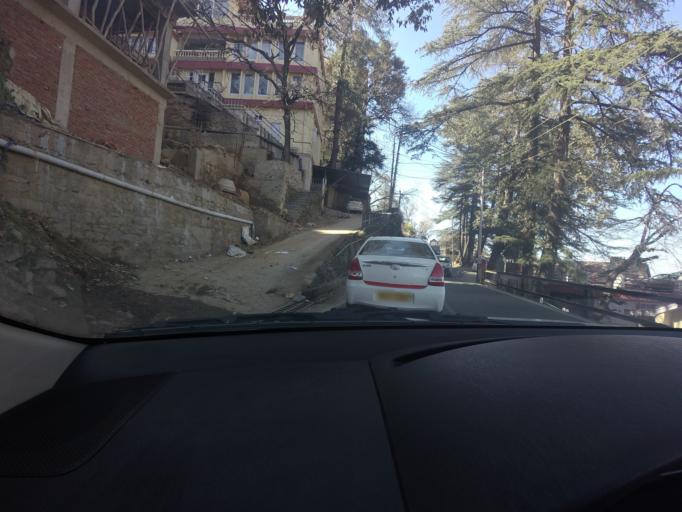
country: IN
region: Himachal Pradesh
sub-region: Shimla
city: Shimla
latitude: 31.1087
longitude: 77.1679
